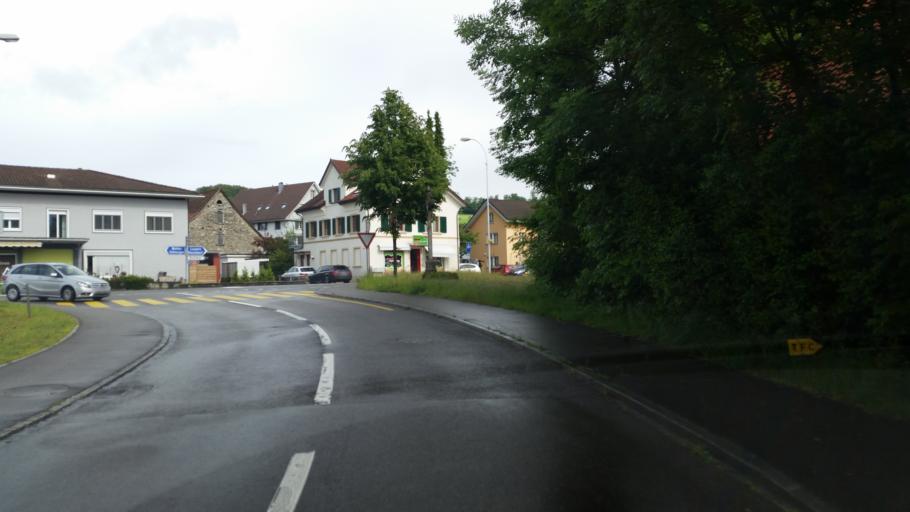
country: CH
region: Aargau
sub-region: Bezirk Bremgarten
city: Sarmenstorf
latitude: 47.3100
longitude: 8.2463
